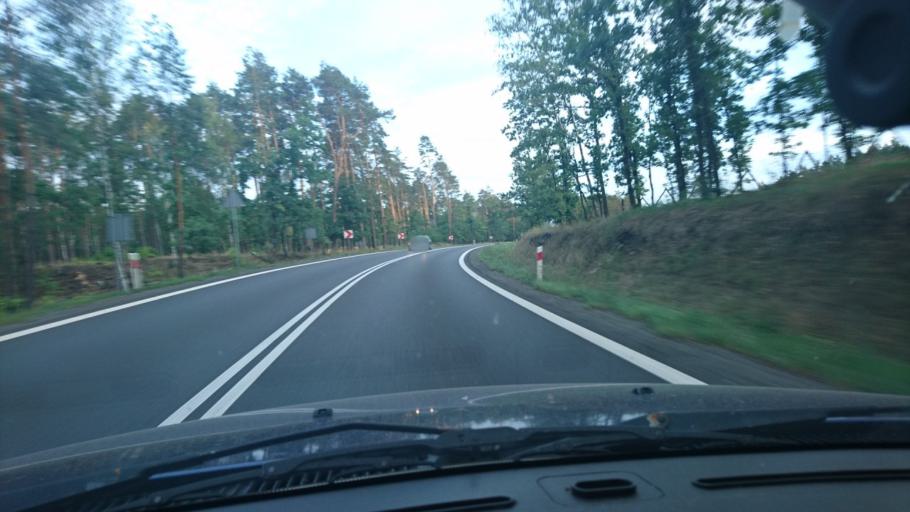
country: PL
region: Silesian Voivodeship
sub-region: Powiat tarnogorski
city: Tworog
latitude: 50.5844
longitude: 18.7067
